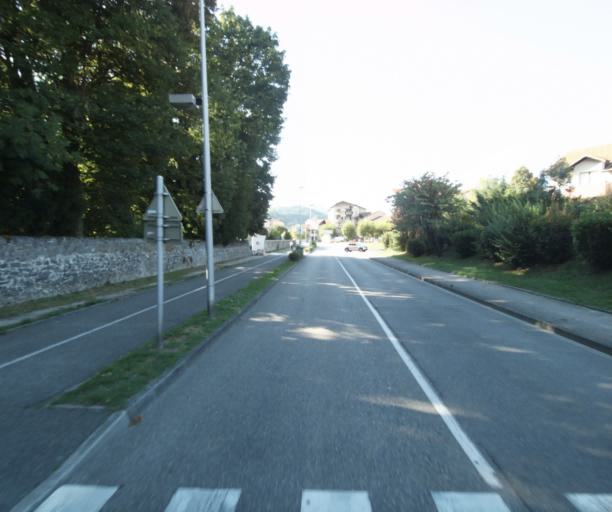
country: FR
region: Rhone-Alpes
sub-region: Departement de l'Isere
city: Sassenage
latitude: 45.2098
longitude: 5.6668
